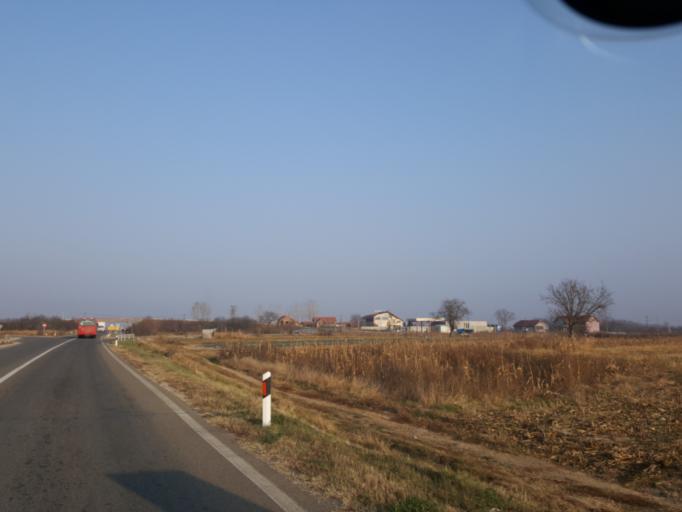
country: RS
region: Central Serbia
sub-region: Jablanicki Okrug
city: Leskovac
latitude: 42.9254
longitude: 22.0182
